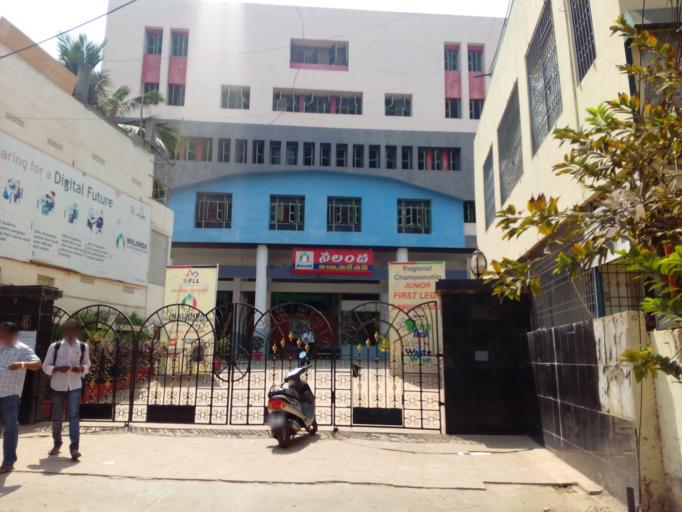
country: IN
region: Andhra Pradesh
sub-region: Krishna
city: Yanamalakuduru
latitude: 16.5020
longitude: 80.6534
